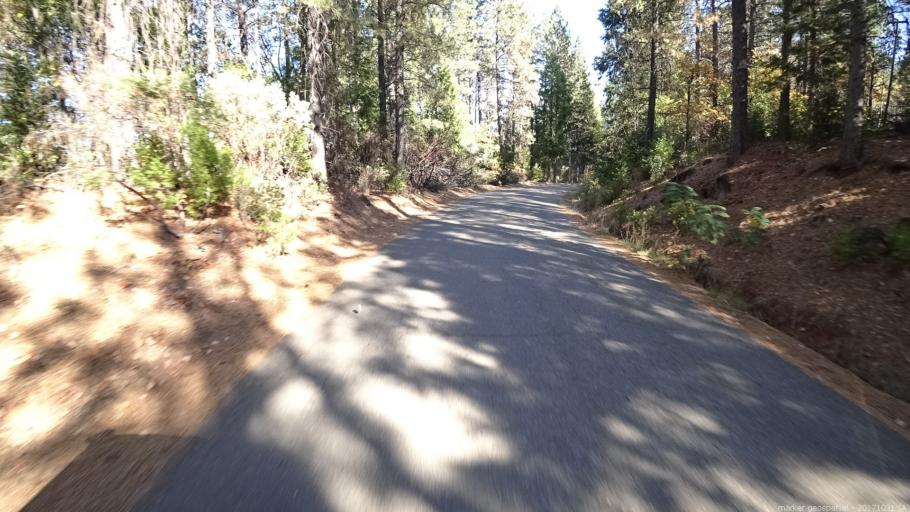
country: US
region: California
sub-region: Shasta County
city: Shingletown
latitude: 40.5109
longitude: -121.9387
